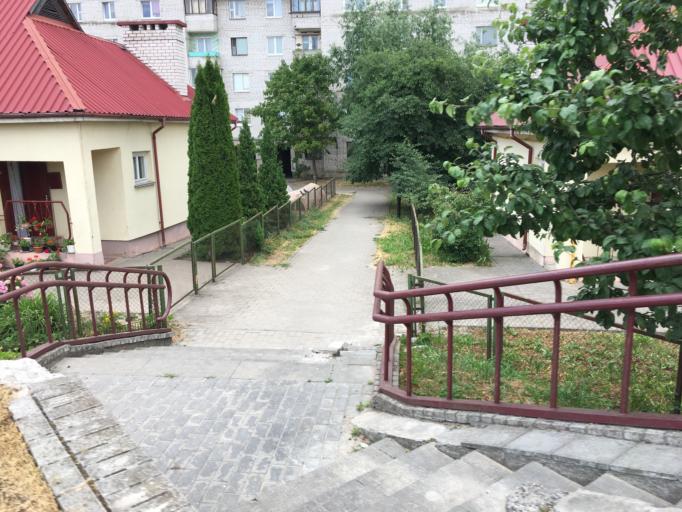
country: BY
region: Grodnenskaya
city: Hrodna
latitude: 53.6995
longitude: 23.8400
